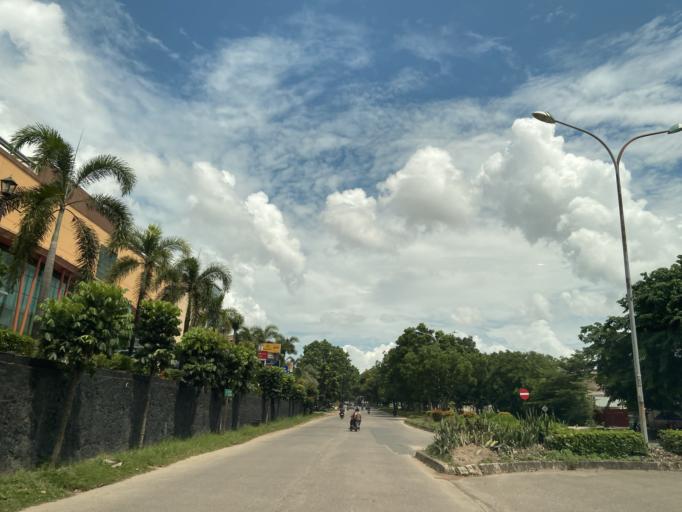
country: SG
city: Singapore
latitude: 1.1414
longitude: 104.0024
